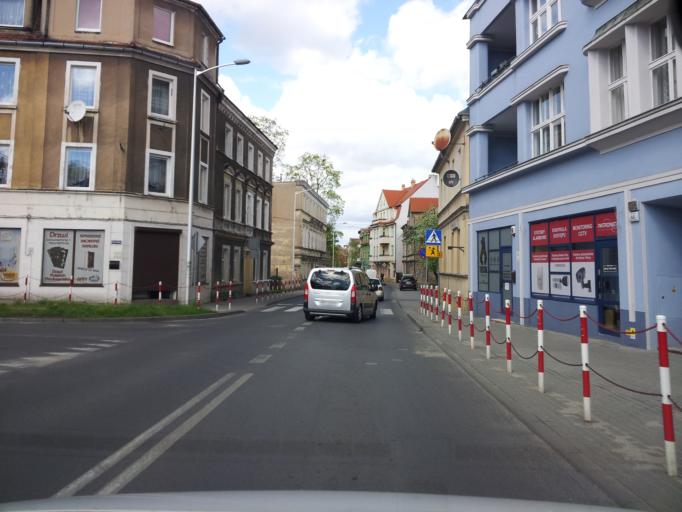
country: PL
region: Lubusz
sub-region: Zielona Gora
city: Zielona Gora
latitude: 51.9324
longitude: 15.5066
